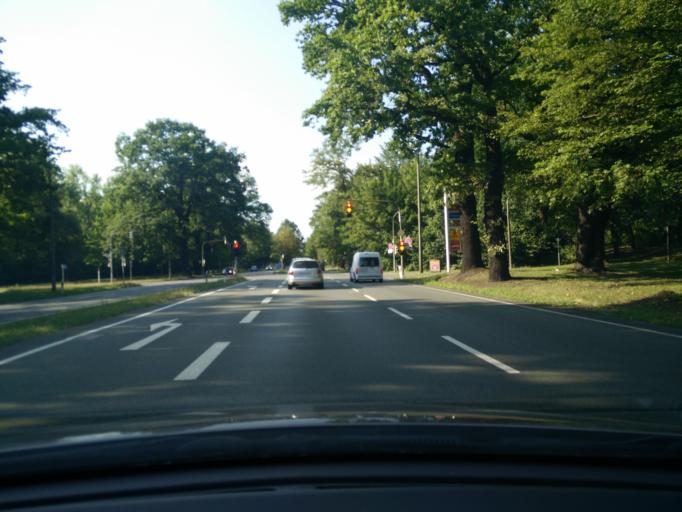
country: DE
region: Bavaria
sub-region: Regierungsbezirk Mittelfranken
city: Nuernberg
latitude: 49.4243
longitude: 11.1050
